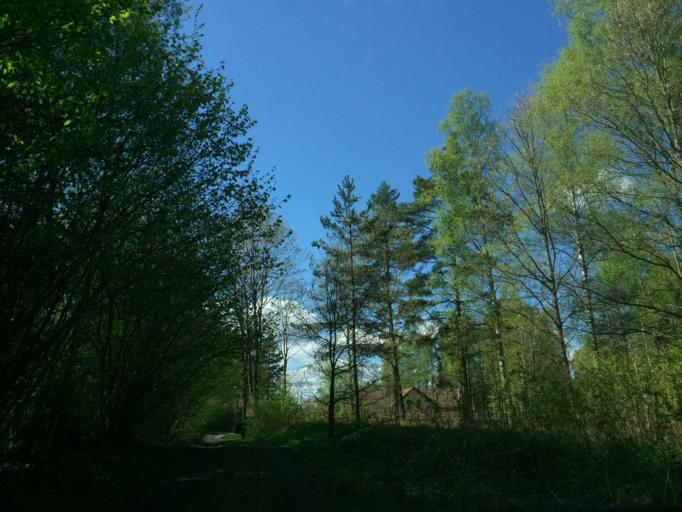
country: LV
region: Baldone
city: Baldone
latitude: 56.7415
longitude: 24.3649
